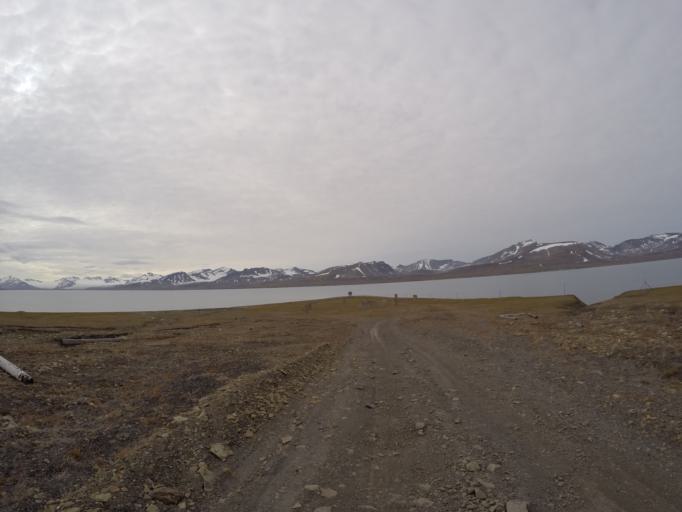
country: SJ
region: Svalbard
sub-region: Spitsbergen
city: Longyearbyen
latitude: 78.0456
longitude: 14.2243
